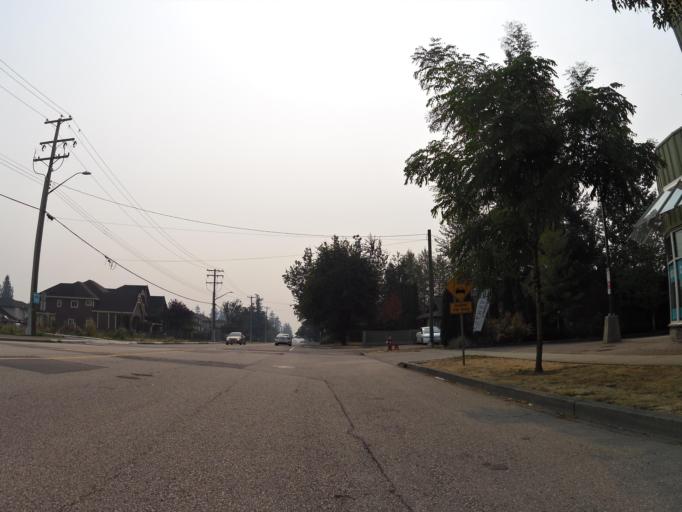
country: CA
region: British Columbia
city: Surrey
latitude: 49.1107
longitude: -122.7567
